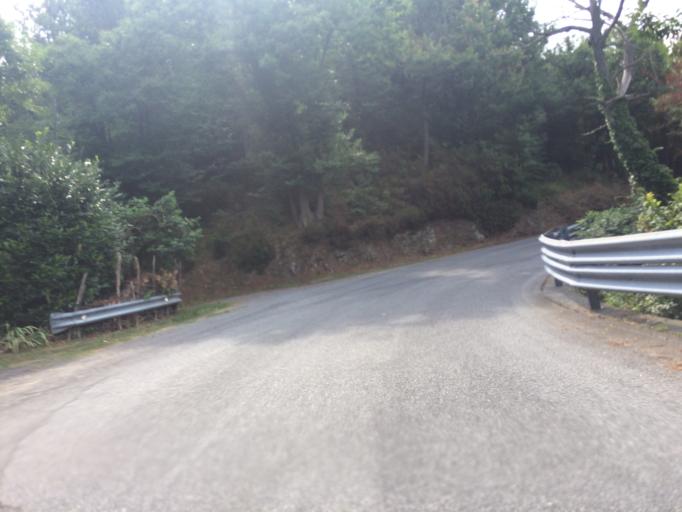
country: IT
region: Liguria
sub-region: Provincia di Savona
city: San Giovanni
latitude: 44.3950
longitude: 8.5042
